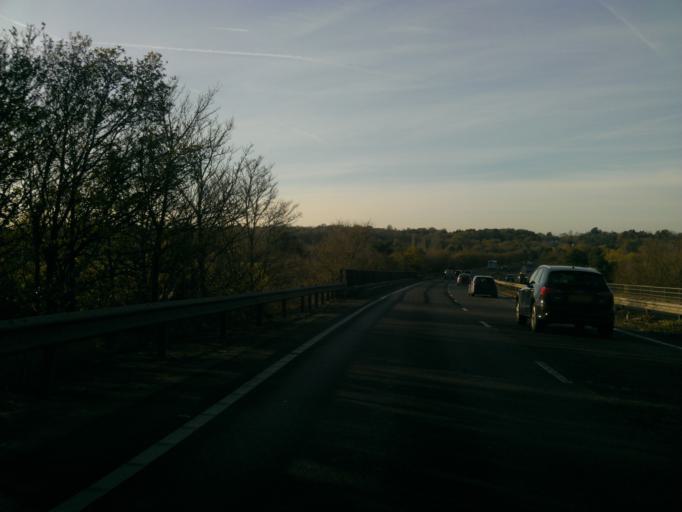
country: GB
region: England
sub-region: Essex
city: West Bergholt
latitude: 51.8996
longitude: 0.8633
